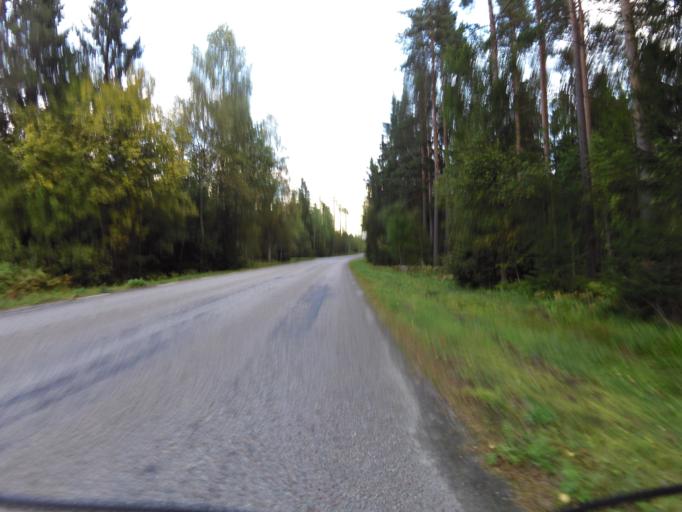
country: SE
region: Gaevleborg
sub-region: Gavle Kommun
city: Valbo
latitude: 60.6674
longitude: 16.9364
